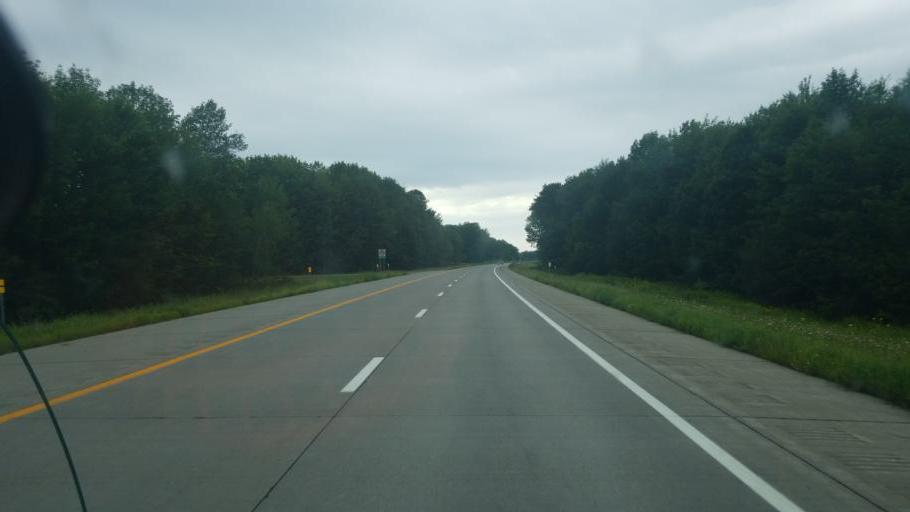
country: US
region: New York
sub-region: Chautauqua County
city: Mayville
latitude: 42.1537
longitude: -79.5131
